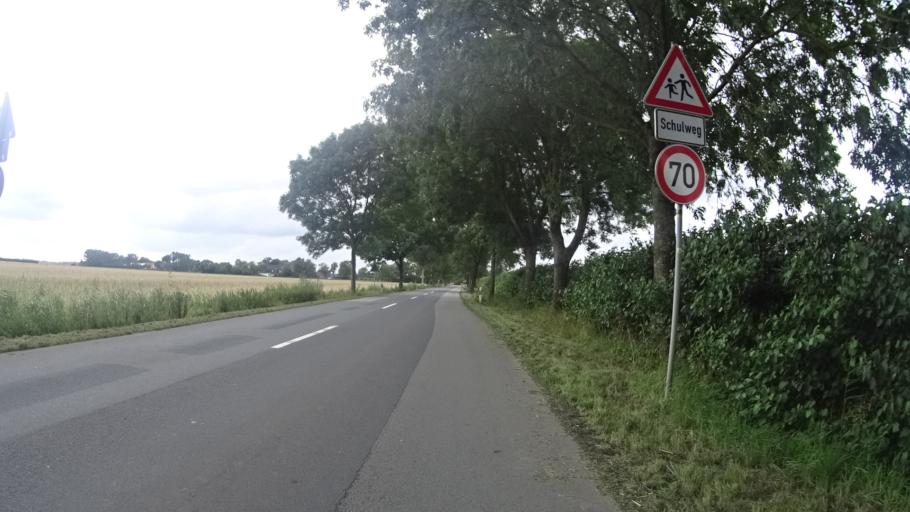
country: DE
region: Lower Saxony
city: Grossenworden
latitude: 53.7025
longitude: 9.2542
